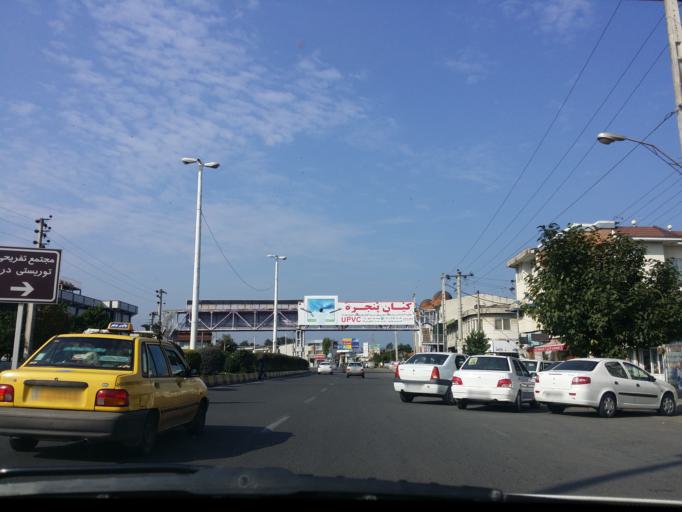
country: IR
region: Mazandaran
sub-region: Nowshahr
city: Nowshahr
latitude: 36.6578
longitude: 51.4823
